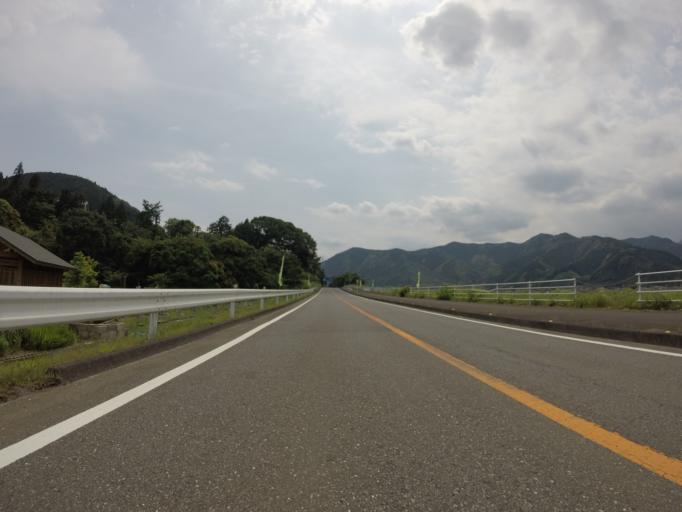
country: JP
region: Shizuoka
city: Shizuoka-shi
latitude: 35.0729
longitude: 138.3720
